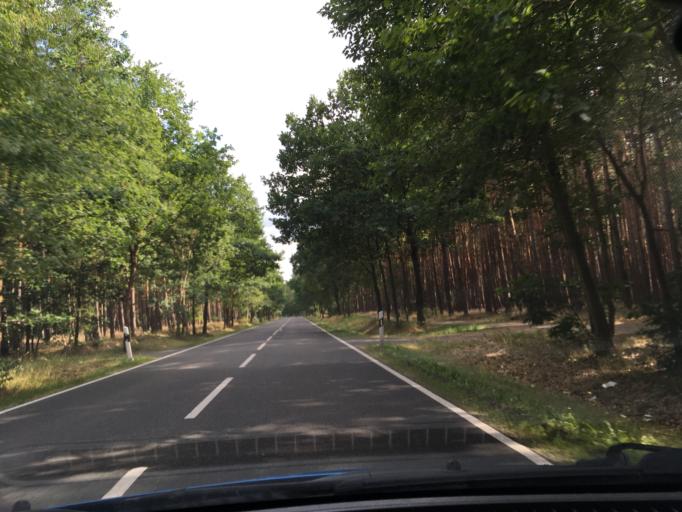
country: DE
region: Mecklenburg-Vorpommern
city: Lubtheen
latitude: 53.2866
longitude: 11.0932
